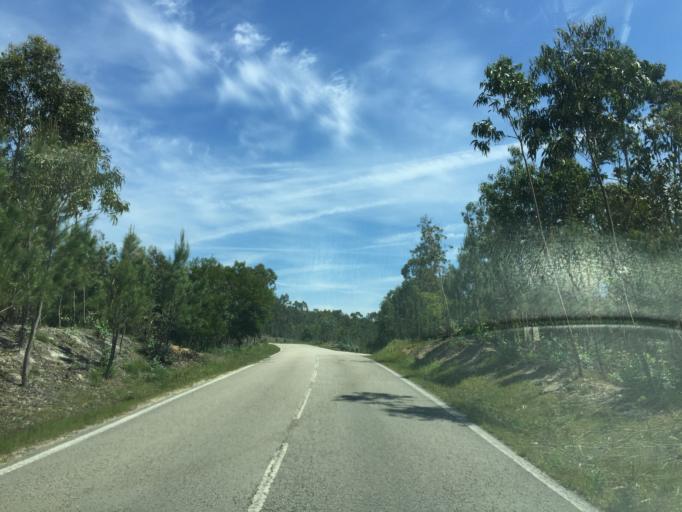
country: PT
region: Leiria
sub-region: Pombal
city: Lourical
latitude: 40.0629
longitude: -8.7071
